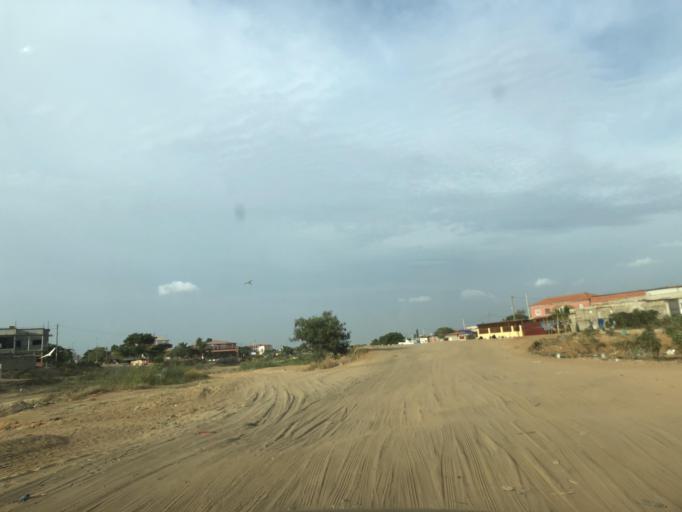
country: AO
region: Luanda
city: Luanda
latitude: -8.9237
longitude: 13.3064
